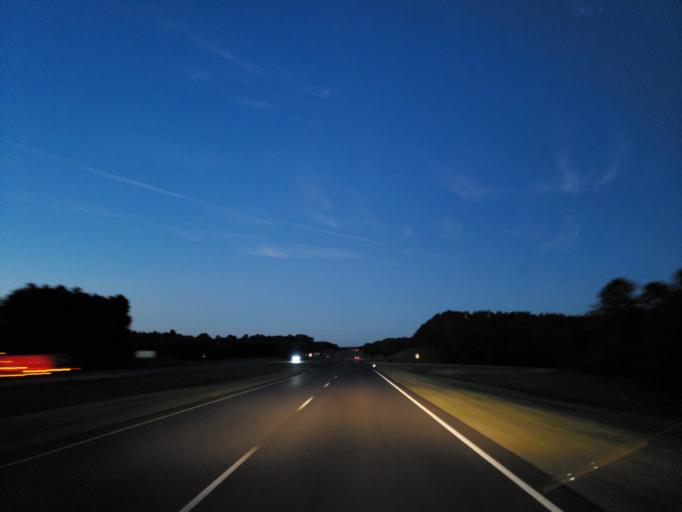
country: US
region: Mississippi
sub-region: Clarke County
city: Quitman
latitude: 32.0111
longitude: -88.6883
